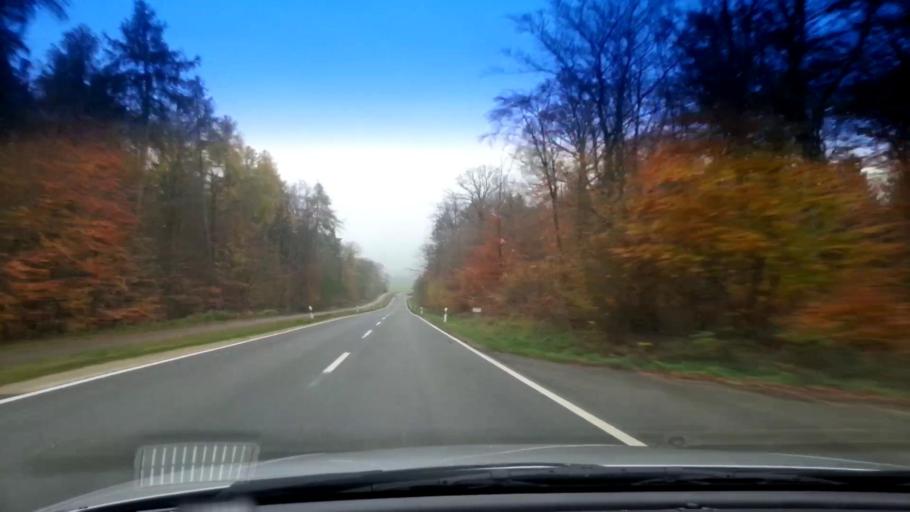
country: DE
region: Bavaria
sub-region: Upper Franconia
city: Litzendorf
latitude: 49.8929
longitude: 11.0087
